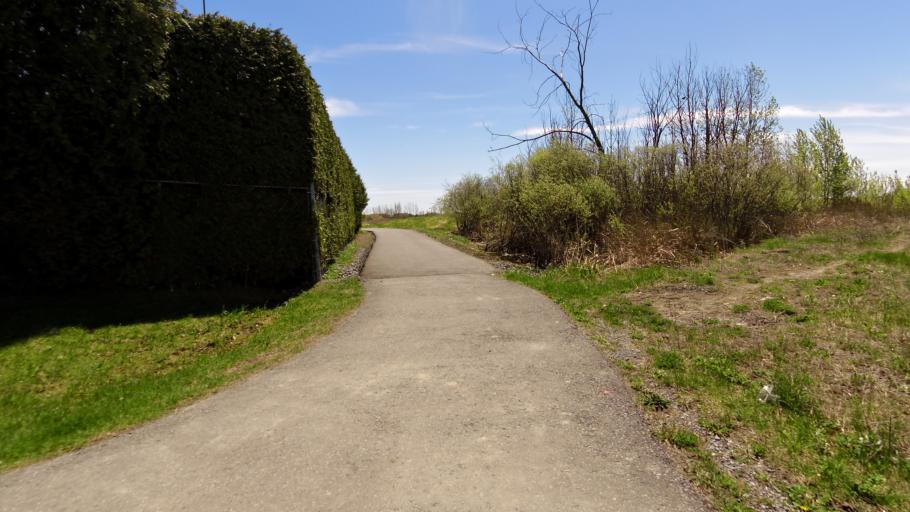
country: CA
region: Ontario
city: Clarence-Rockland
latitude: 45.4592
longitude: -75.4826
